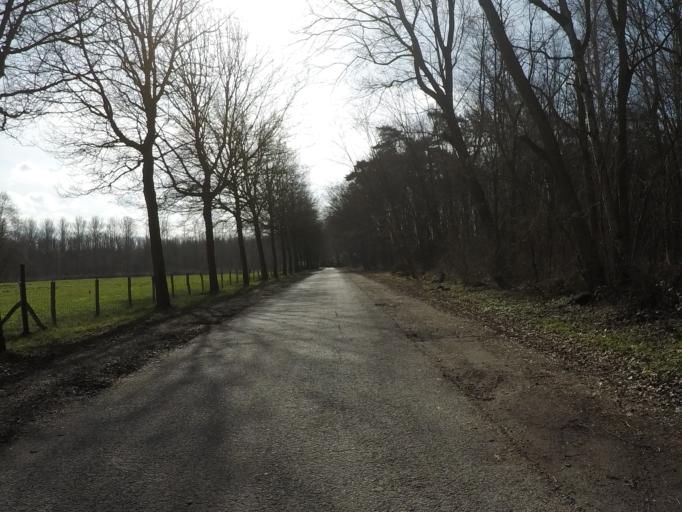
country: BE
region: Flanders
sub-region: Provincie Antwerpen
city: Ranst
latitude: 51.2008
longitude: 4.5624
